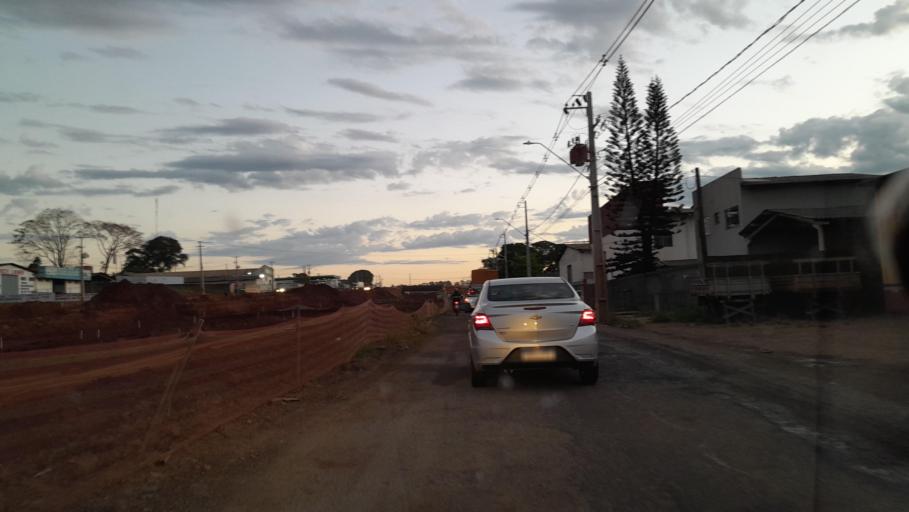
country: BR
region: Parana
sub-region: Umuarama
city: Umuarama
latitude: -23.7861
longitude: -53.3118
